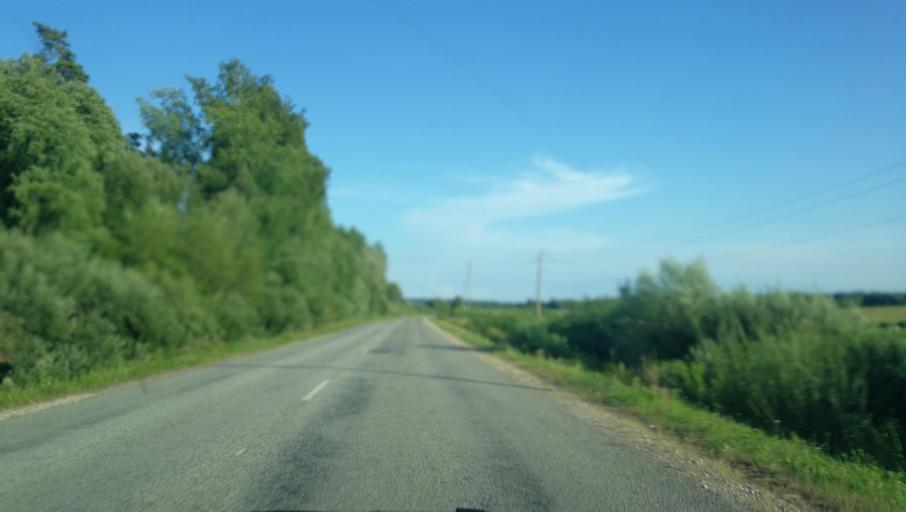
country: LV
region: Cesu Rajons
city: Cesis
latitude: 57.2902
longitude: 25.3089
